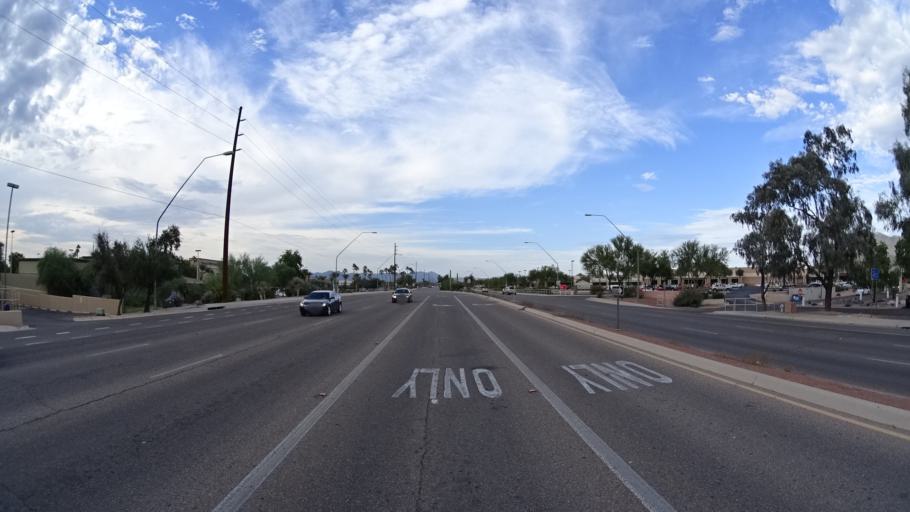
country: US
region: Arizona
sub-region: Pima County
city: Casas Adobes
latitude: 32.3380
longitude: -111.0128
